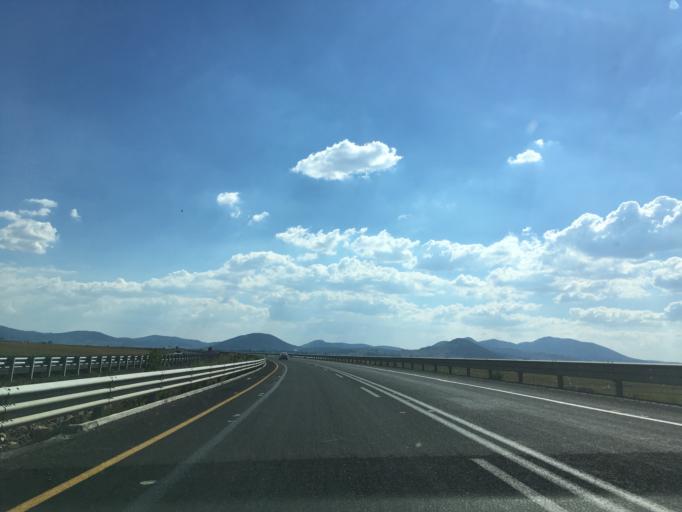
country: MX
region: Mexico
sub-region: Timilpan
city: Tercera Manzana de Zaragoza
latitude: 19.9602
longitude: -99.6957
